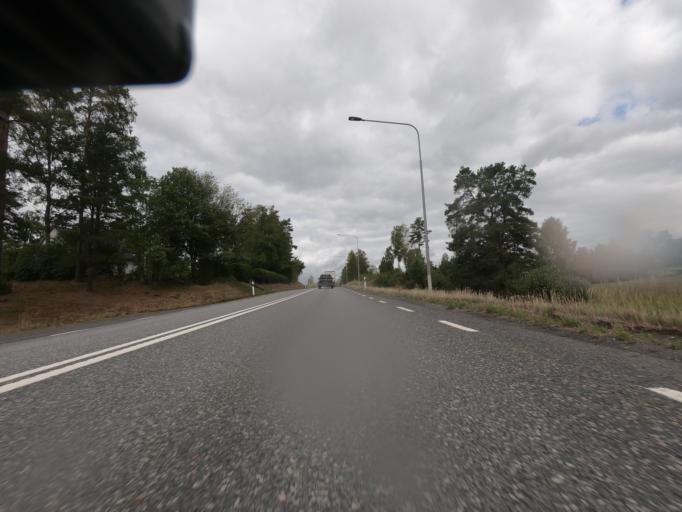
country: SE
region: Joenkoeping
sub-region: Vaggeryds Kommun
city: Vaggeryd
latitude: 57.4733
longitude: 14.3163
